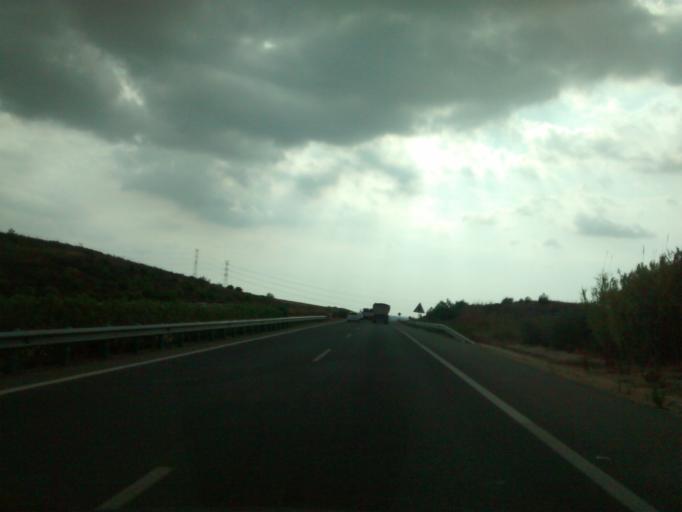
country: ES
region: Andalusia
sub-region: Provincia de Cadiz
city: Arcos de la Frontera
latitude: 36.7691
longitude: -5.8378
